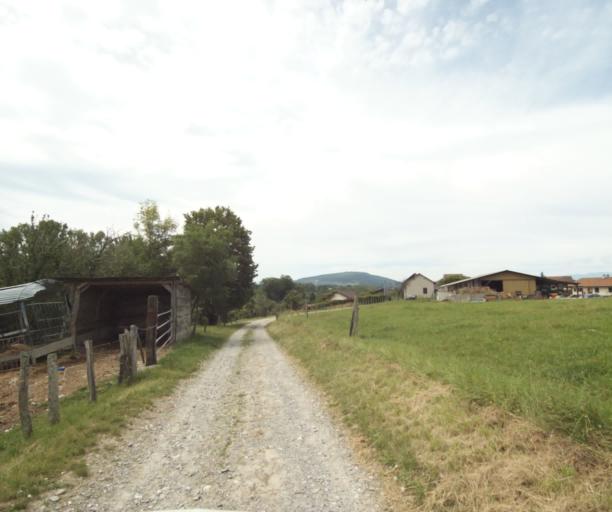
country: FR
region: Rhone-Alpes
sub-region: Departement de la Haute-Savoie
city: Margencel
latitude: 46.3394
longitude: 6.4243
